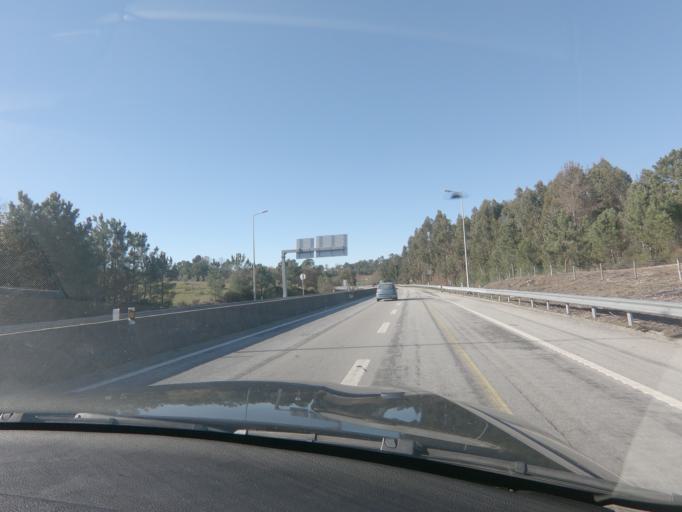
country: PT
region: Viseu
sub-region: Viseu
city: Abraveses
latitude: 40.6741
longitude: -7.9756
